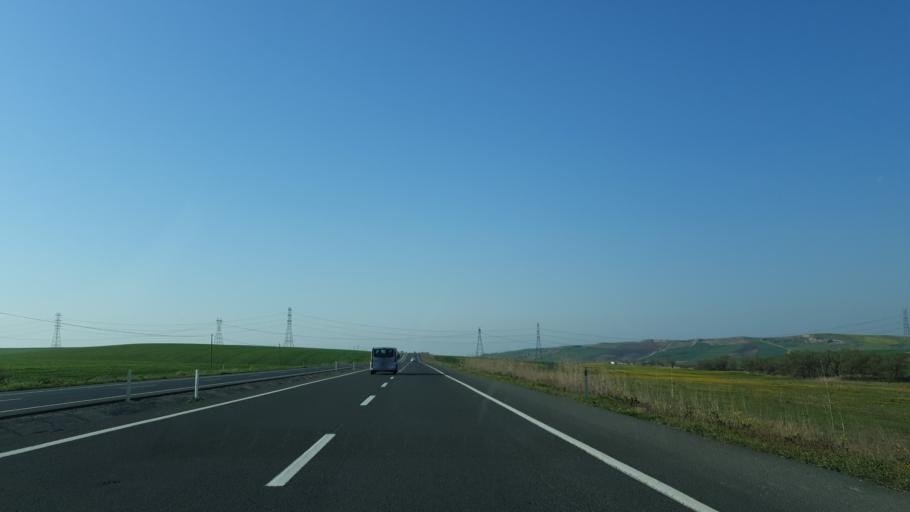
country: TR
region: Tekirdag
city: Corlu
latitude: 41.0801
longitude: 27.7418
